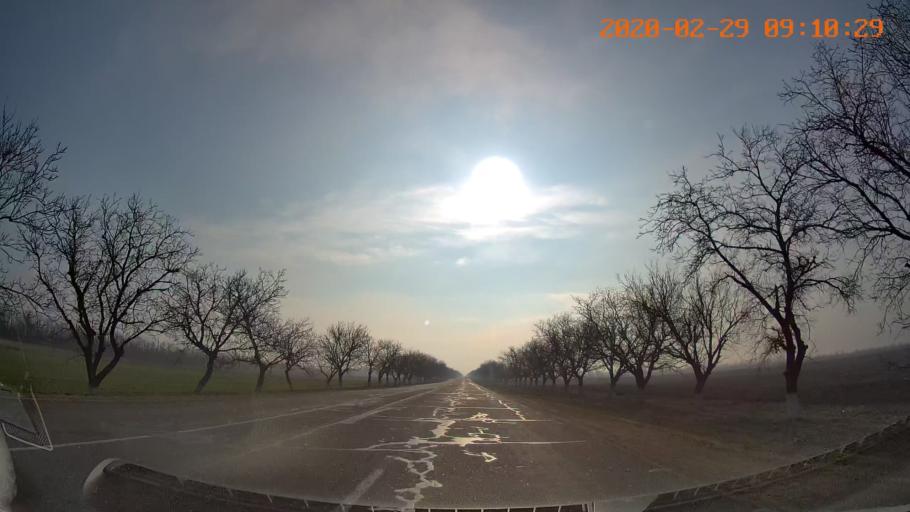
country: MD
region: Telenesti
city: Slobozia
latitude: 46.8436
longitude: 29.7830
